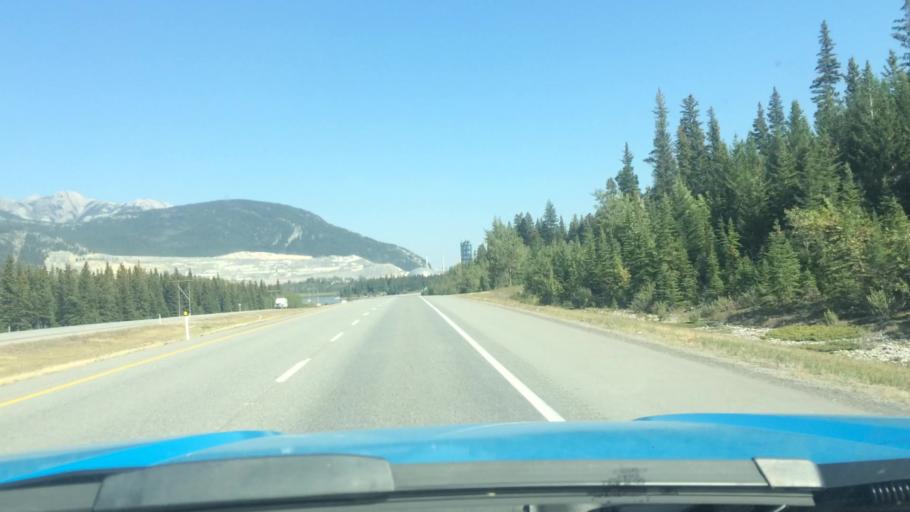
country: CA
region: Alberta
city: Canmore
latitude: 51.0514
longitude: -115.2126
